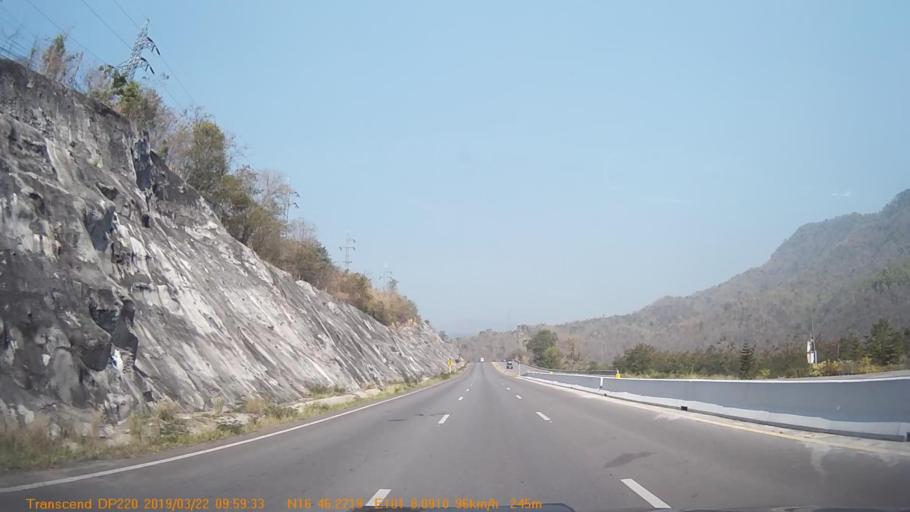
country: TH
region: Phetchabun
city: Lom Sak
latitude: 16.7716
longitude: 101.1343
